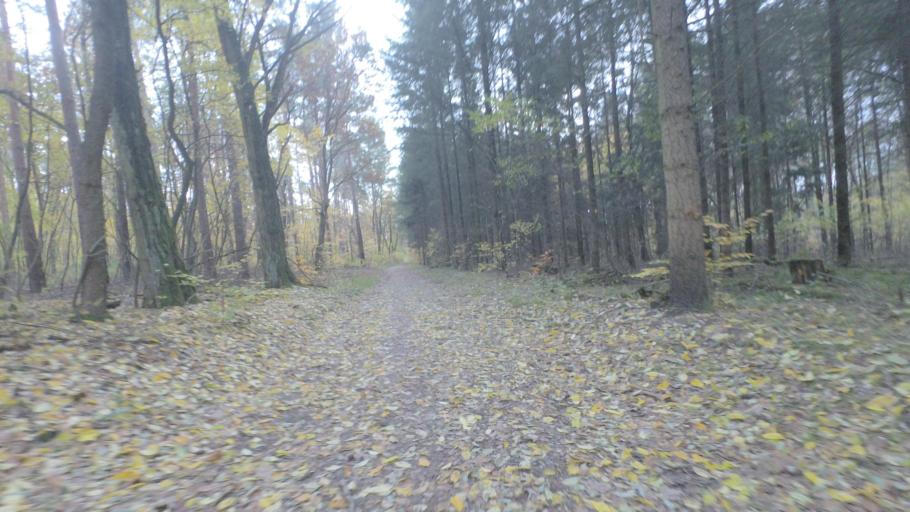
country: DE
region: Brandenburg
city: Rangsdorf
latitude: 52.3095
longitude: 13.4200
